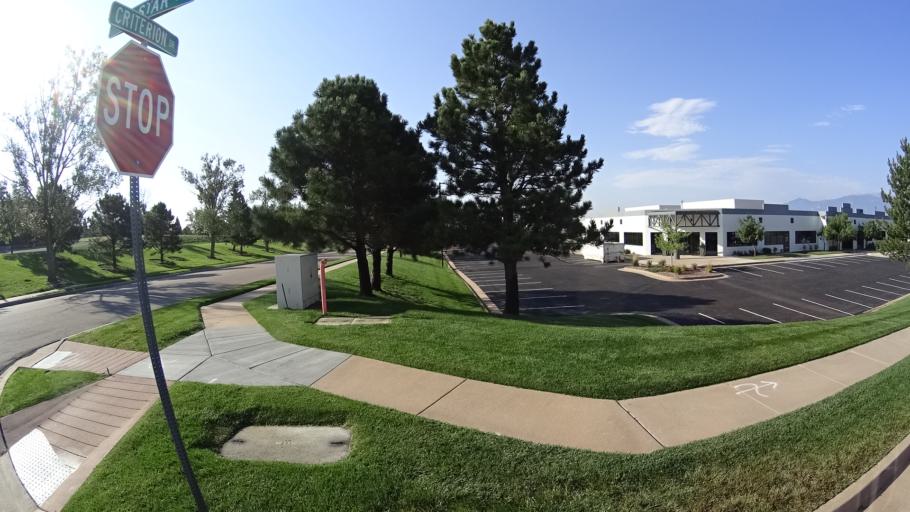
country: US
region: Colorado
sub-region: El Paso County
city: Air Force Academy
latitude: 38.9588
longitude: -104.7882
